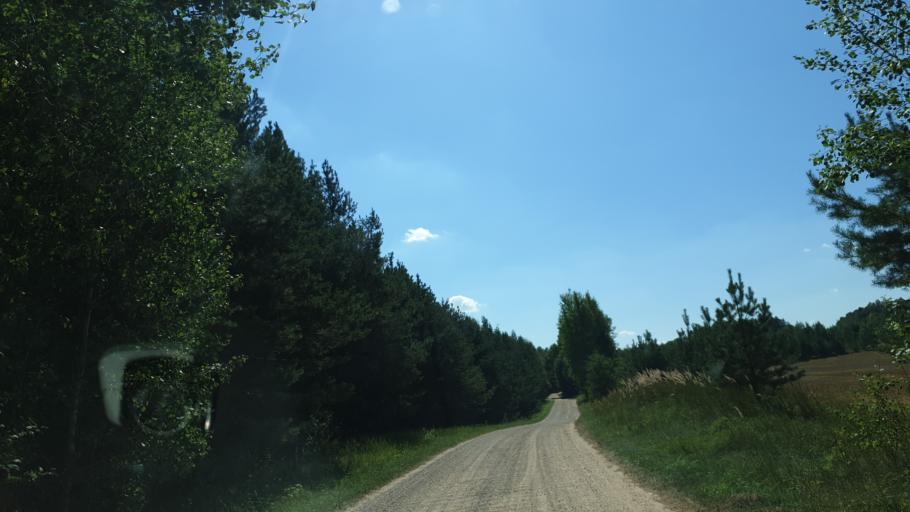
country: LT
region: Vilnius County
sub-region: Vilniaus Rajonas
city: Vievis
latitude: 54.9027
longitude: 24.8786
